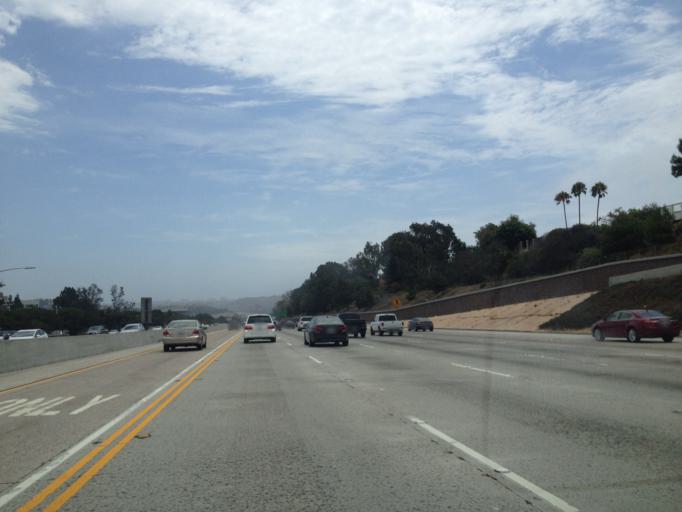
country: US
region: California
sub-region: San Diego County
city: Del Mar
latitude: 32.9479
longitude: -117.2434
